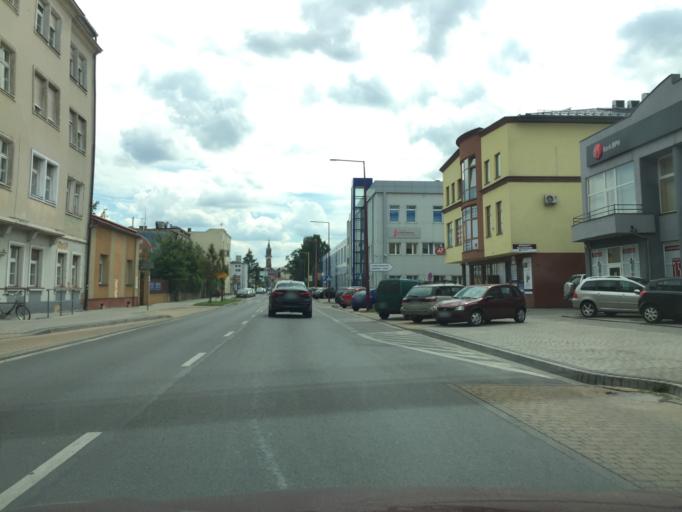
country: PL
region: Greater Poland Voivodeship
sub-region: Kalisz
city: Kalisz
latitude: 51.7547
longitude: 18.0941
